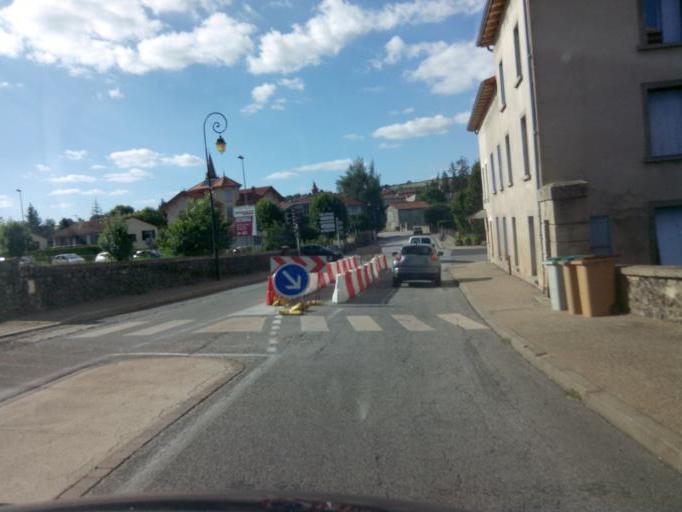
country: FR
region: Auvergne
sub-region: Departement de la Haute-Loire
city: Saint-Paulien
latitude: 45.1318
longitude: 3.8159
